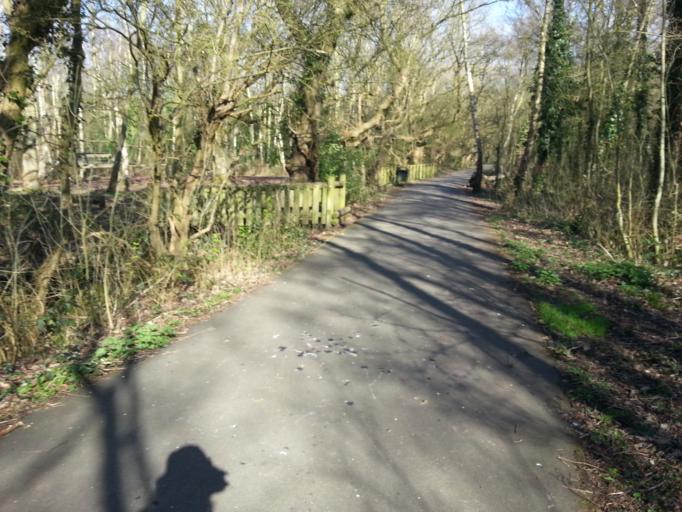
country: GB
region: England
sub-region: Knowsley
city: Huyton
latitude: 53.3663
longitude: -2.8427
